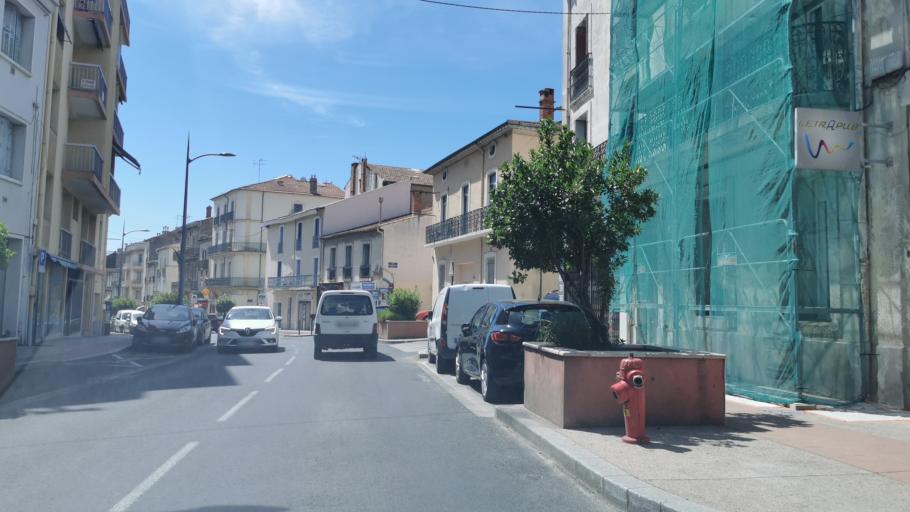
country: FR
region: Languedoc-Roussillon
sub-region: Departement de l'Herault
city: Beziers
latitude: 43.3410
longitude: 3.2222
